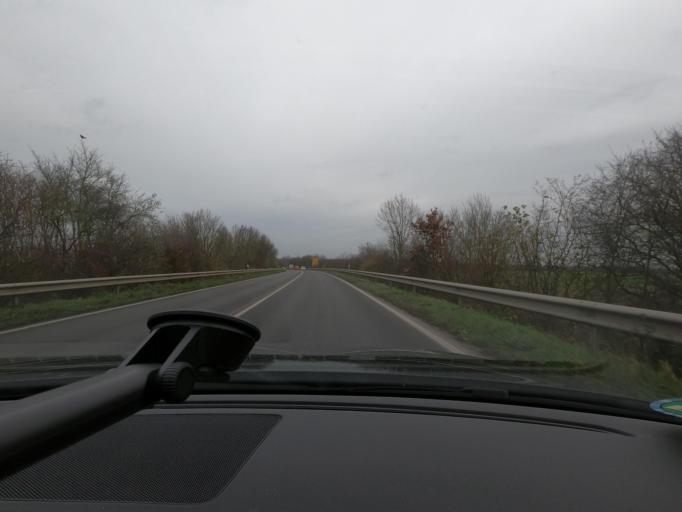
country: DE
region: North Rhine-Westphalia
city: Kempen
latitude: 51.3606
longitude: 6.4430
